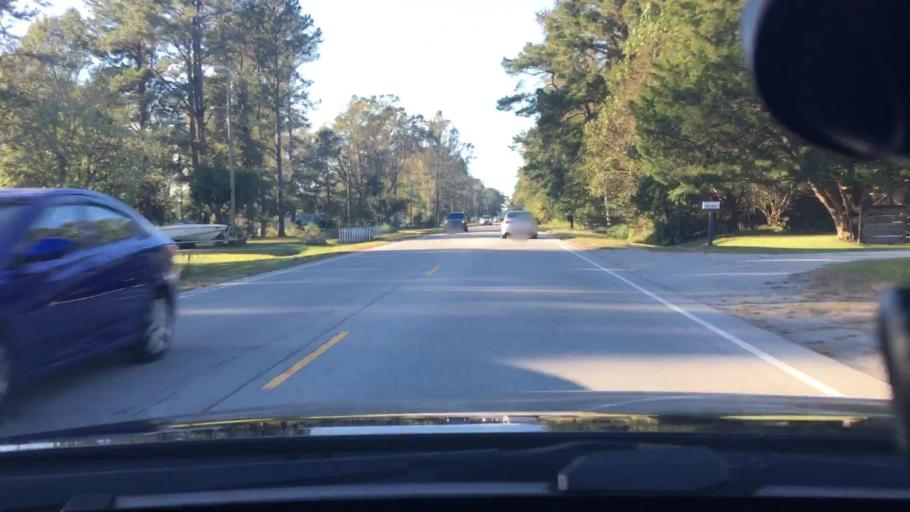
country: US
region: North Carolina
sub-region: Craven County
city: Vanceboro
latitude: 35.2584
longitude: -77.0984
